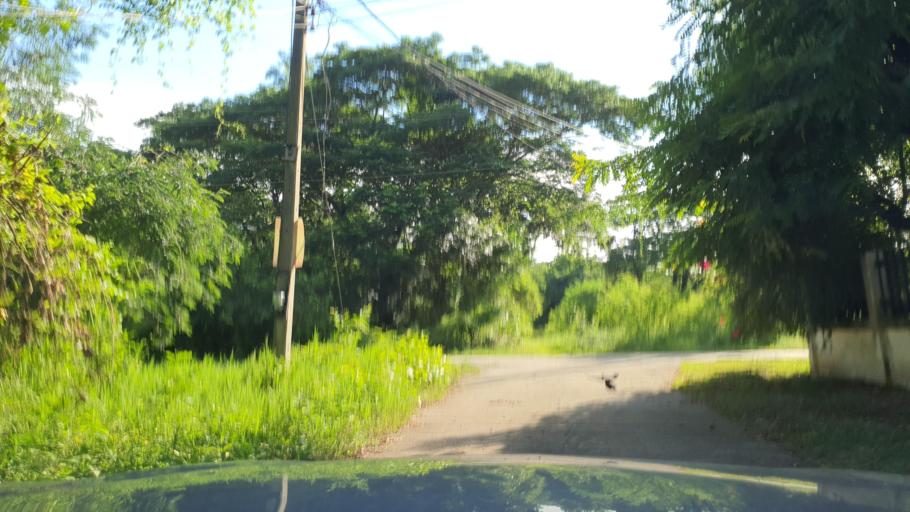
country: TH
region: Chiang Mai
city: San Kamphaeng
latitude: 18.7491
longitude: 99.1028
